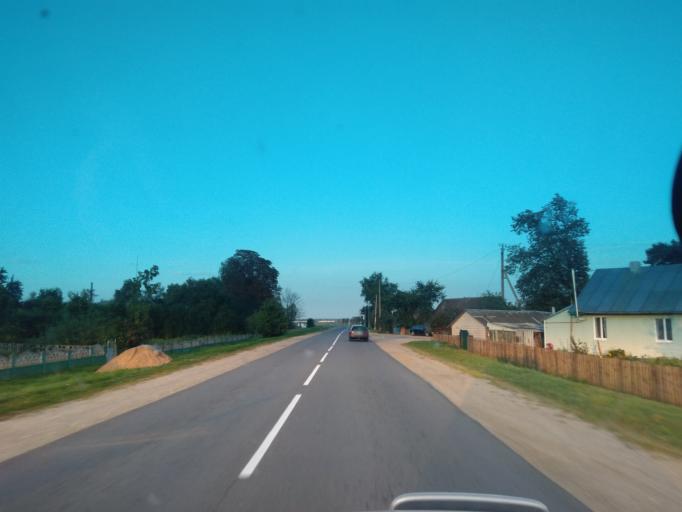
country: BY
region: Minsk
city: Slutsk
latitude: 53.1500
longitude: 27.5471
